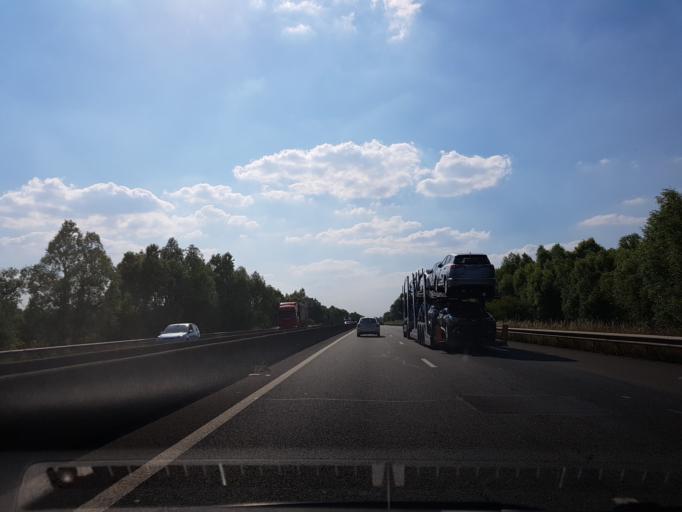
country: FR
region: Nord-Pas-de-Calais
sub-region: Departement du Nord
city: Lallaing
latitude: 50.3784
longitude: 3.1610
